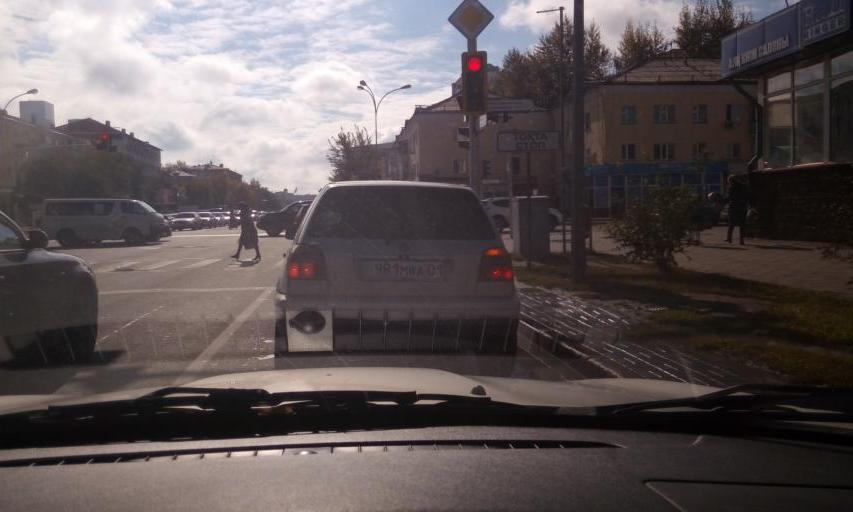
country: KZ
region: Astana Qalasy
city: Astana
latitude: 51.1702
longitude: 71.4126
